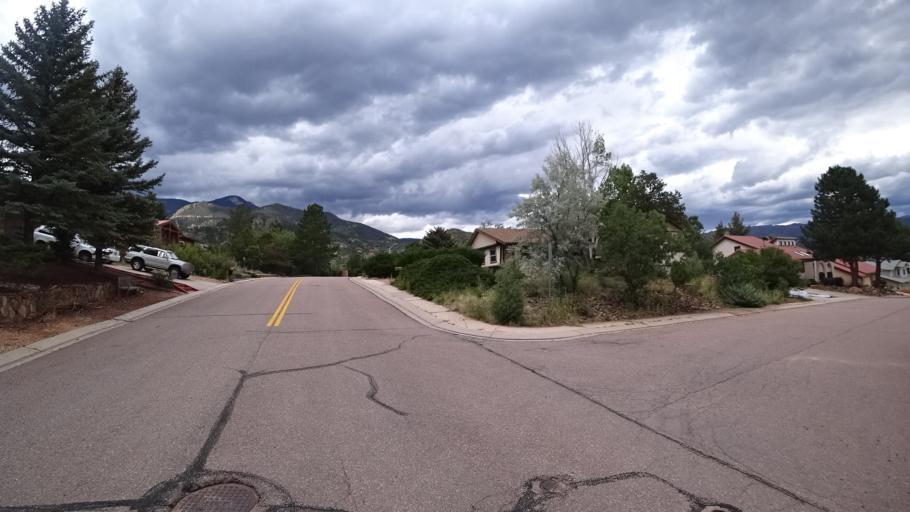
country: US
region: Colorado
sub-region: El Paso County
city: Manitou Springs
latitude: 38.8431
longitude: -104.8968
